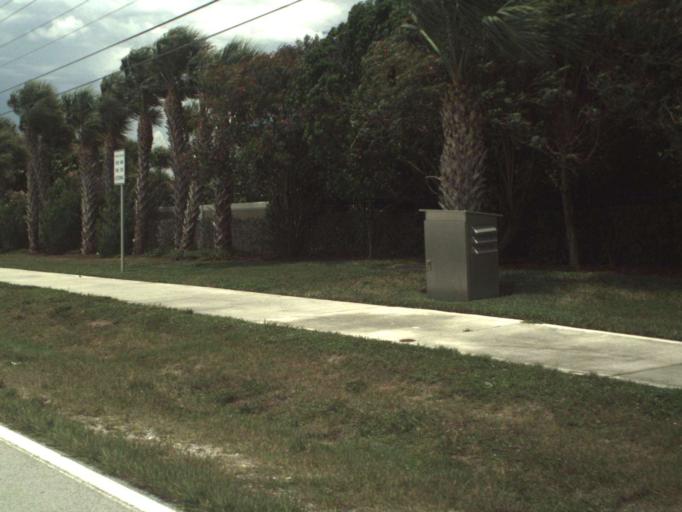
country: US
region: Florida
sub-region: Saint Lucie County
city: Hutchinson Island South
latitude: 27.3204
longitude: -80.2274
